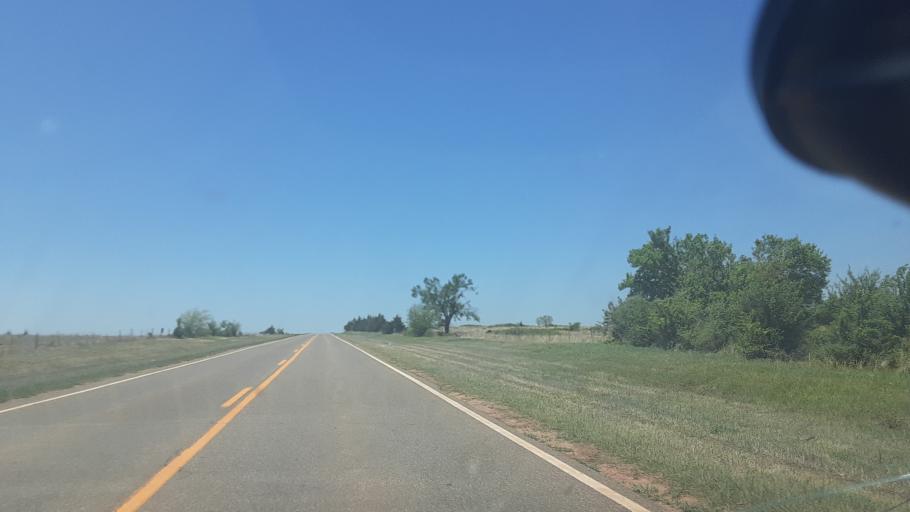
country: US
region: Oklahoma
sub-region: Noble County
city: Perry
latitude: 36.1157
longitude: -97.3567
